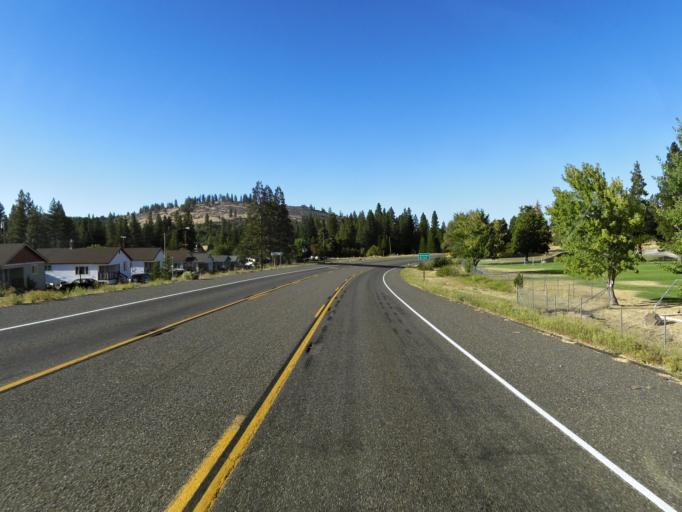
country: US
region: California
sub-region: Siskiyou County
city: Weed
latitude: 41.4372
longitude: -122.3873
